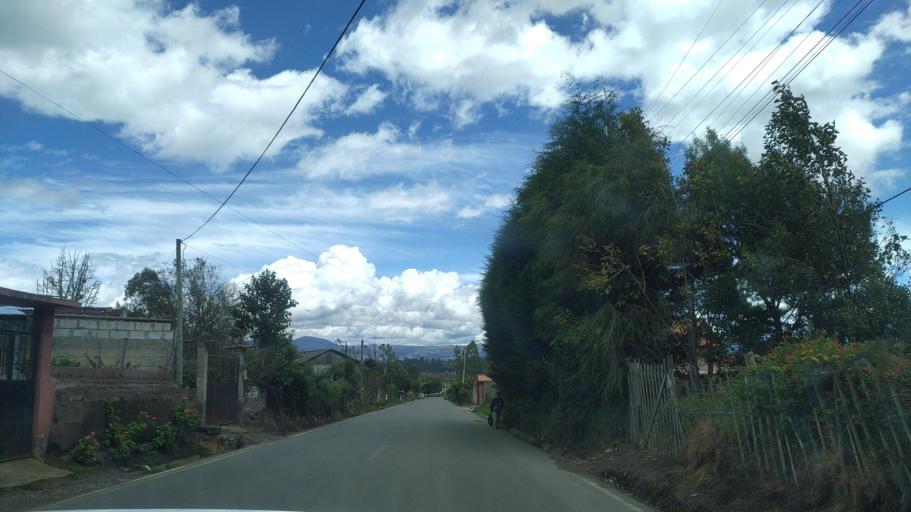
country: EC
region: Chimborazo
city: Riobamba
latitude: -1.6587
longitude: -78.5745
